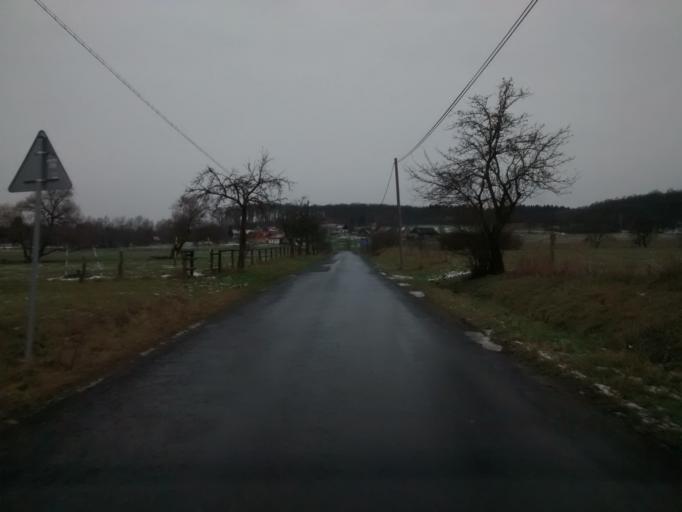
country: CZ
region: Central Bohemia
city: Rozd'alovice
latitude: 50.3252
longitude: 15.1760
